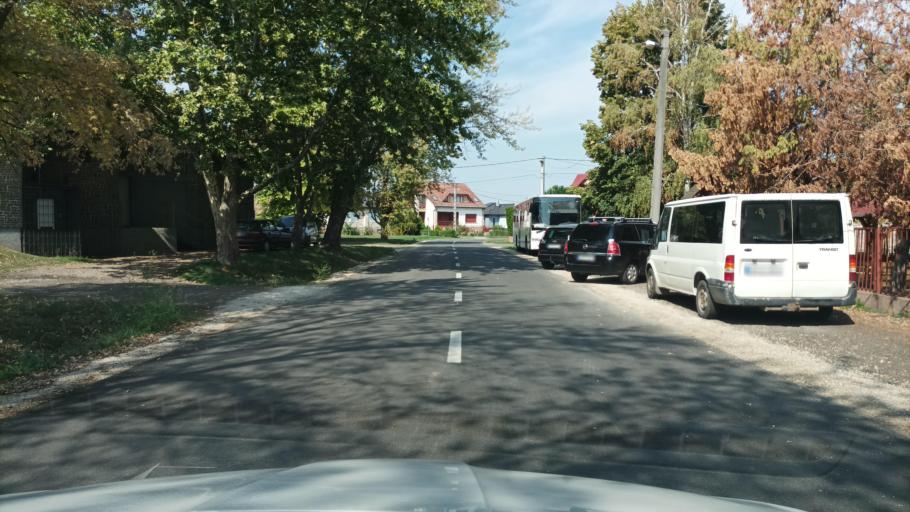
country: HU
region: Pest
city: Galgaheviz
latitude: 47.6227
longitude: 19.5530
